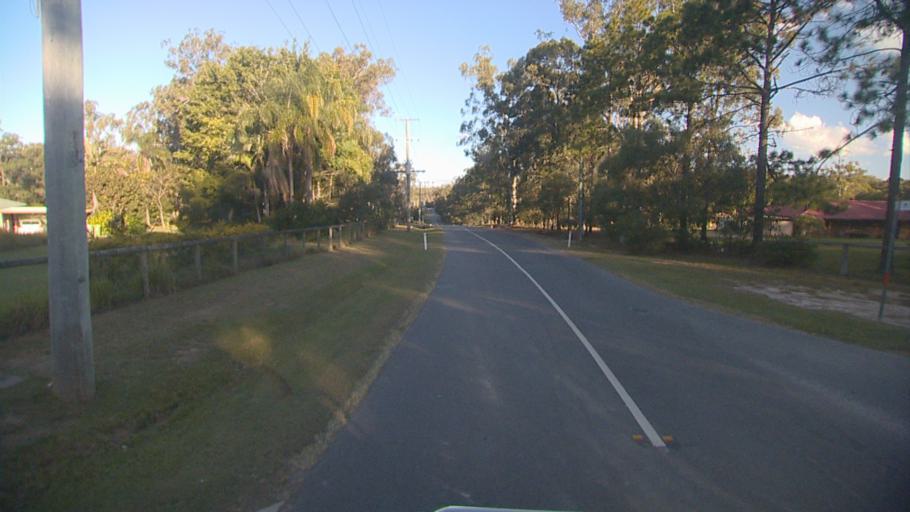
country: AU
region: Queensland
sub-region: Redland
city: Redland Bay
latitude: -27.6687
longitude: 153.2740
